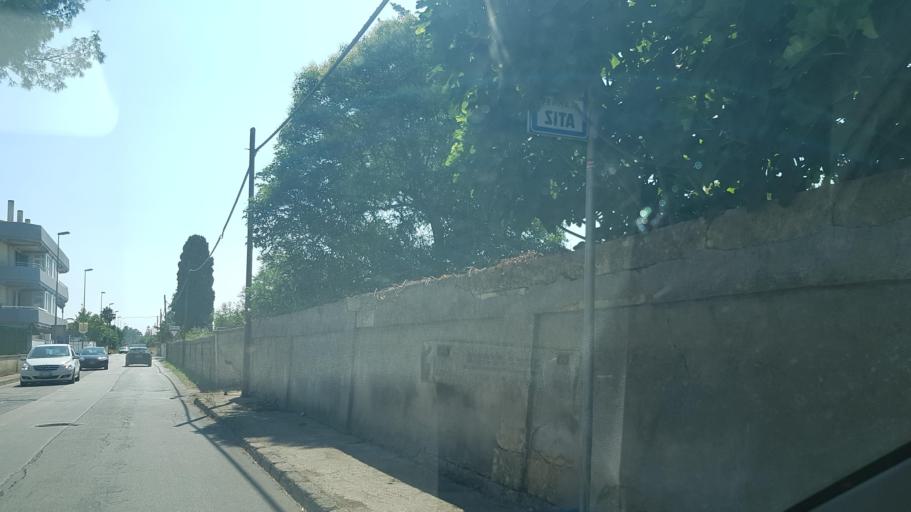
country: IT
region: Apulia
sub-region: Provincia di Lecce
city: Taurisano
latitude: 39.9552
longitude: 18.2084
